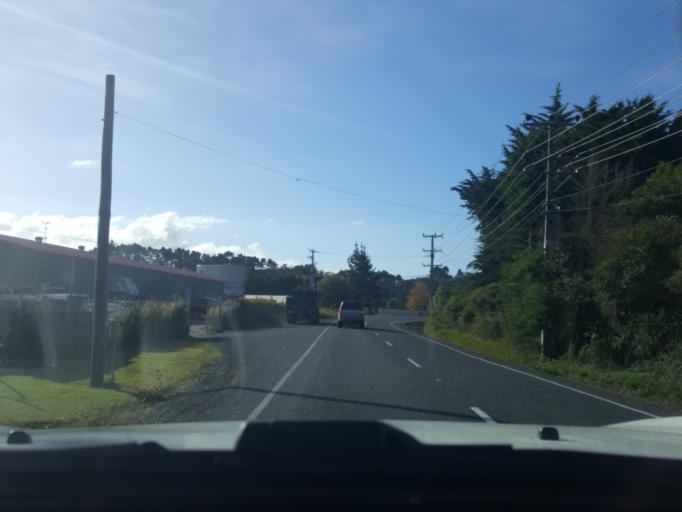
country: NZ
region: Auckland
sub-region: Auckland
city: Muriwai Beach
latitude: -36.7640
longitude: 174.5769
